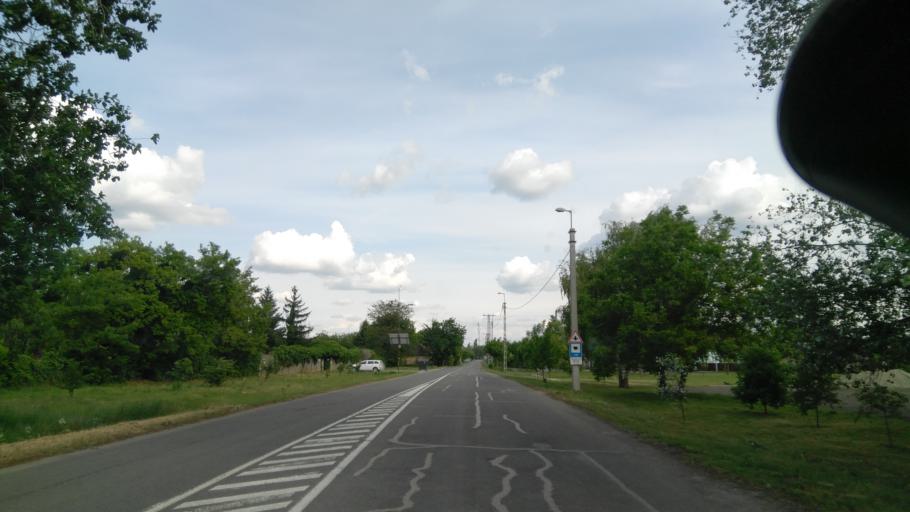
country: HU
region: Bekes
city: Battonya
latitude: 46.2858
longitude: 21.0357
